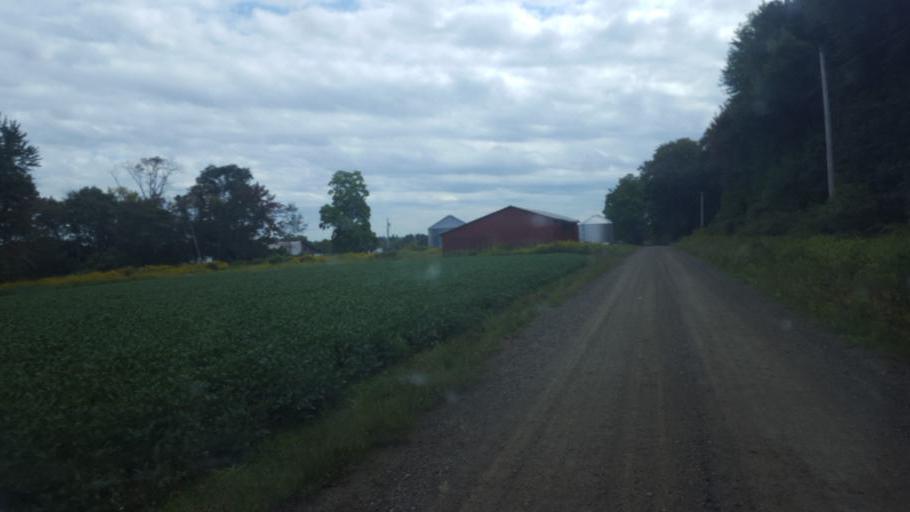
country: US
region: Pennsylvania
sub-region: Crawford County
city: Pymatuning Central
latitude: 41.5264
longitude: -80.4024
